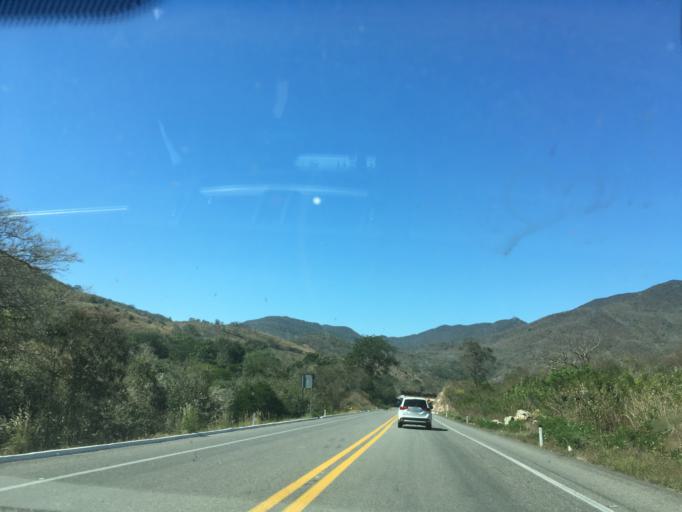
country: MX
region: Michoacan
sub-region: Arteaga
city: Infiernillo (Morelos de Infiernillo)
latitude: 18.1736
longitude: -101.9067
